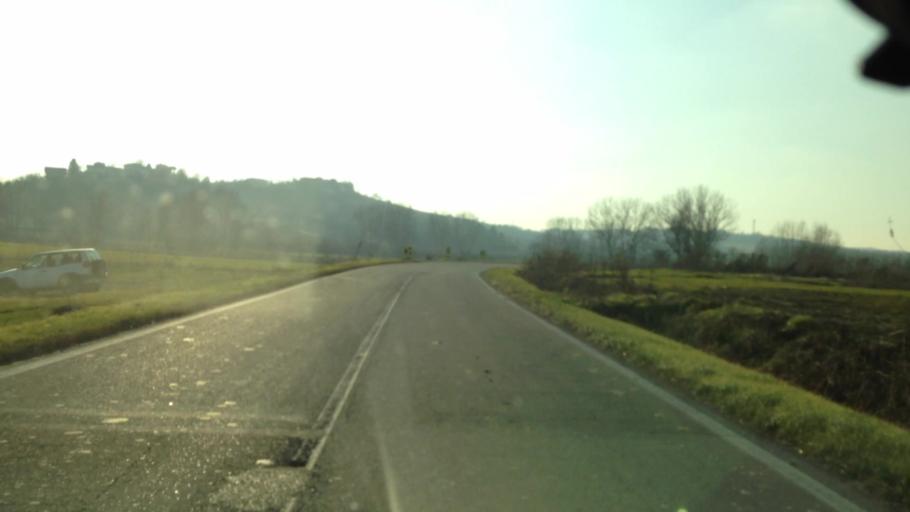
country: IT
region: Piedmont
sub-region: Provincia di Asti
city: Montaldo Scarampi
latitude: 44.8179
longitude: 8.2738
